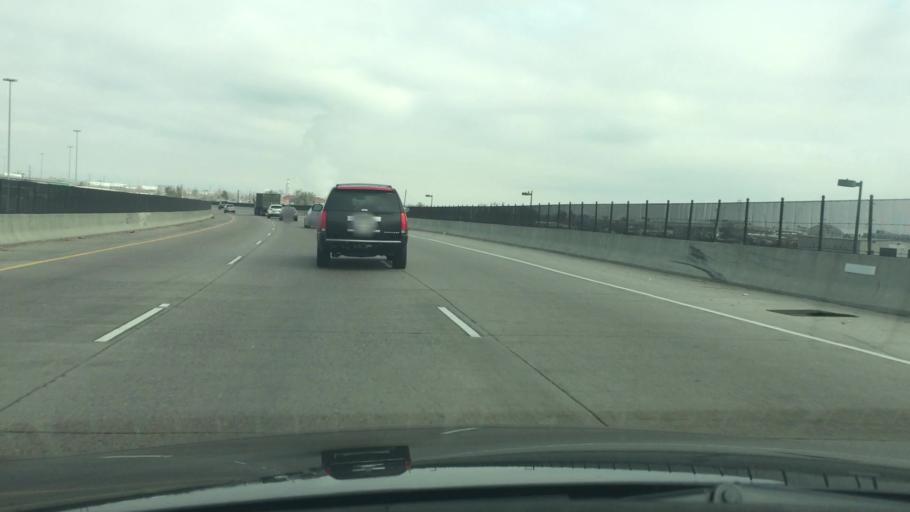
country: US
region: Colorado
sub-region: Denver County
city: Denver
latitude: 39.7705
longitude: -104.9907
